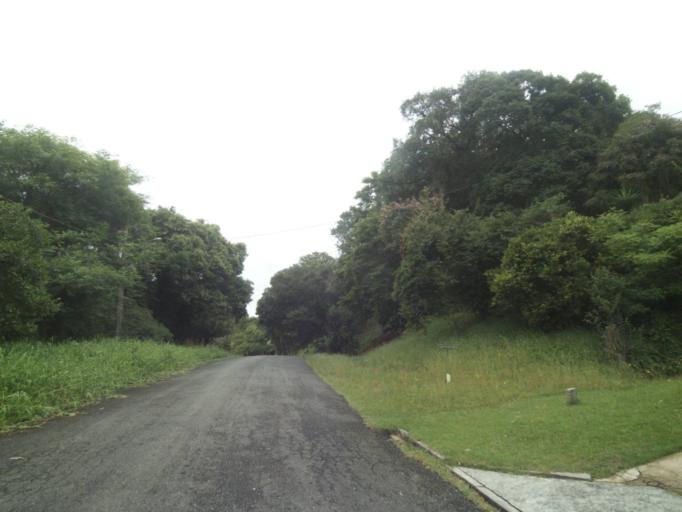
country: BR
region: Parana
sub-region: Curitiba
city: Curitiba
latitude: -25.4084
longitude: -49.2879
